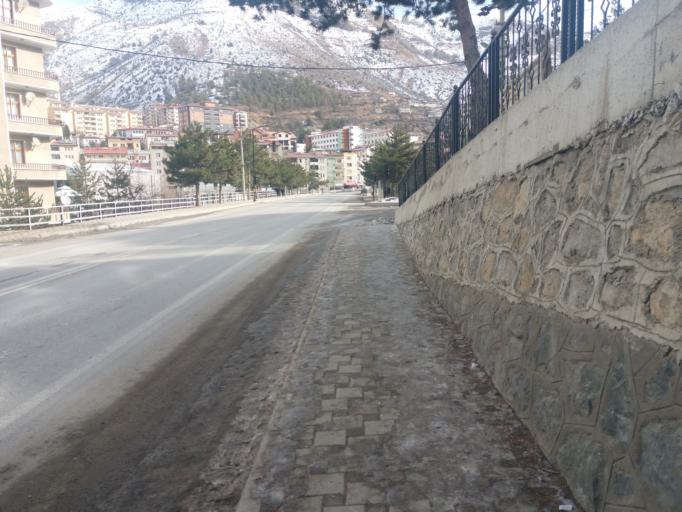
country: TR
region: Gumushane
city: Gumushkhane
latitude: 40.4575
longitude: 39.4838
